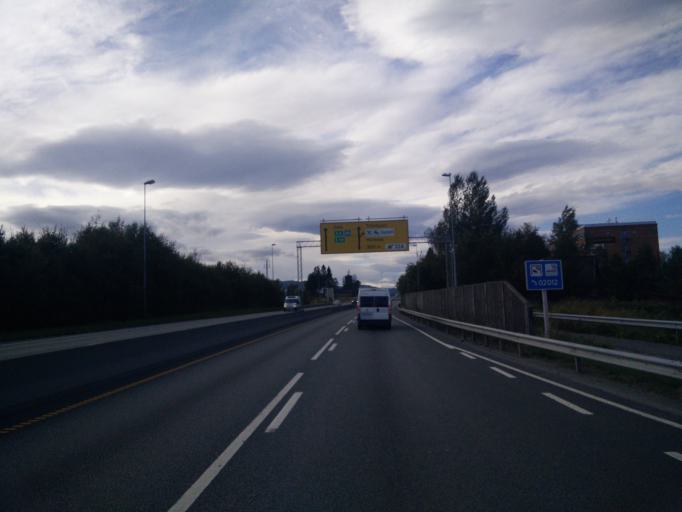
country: NO
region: Sor-Trondelag
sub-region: Trondheim
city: Trondheim
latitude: 63.3685
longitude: 10.3791
